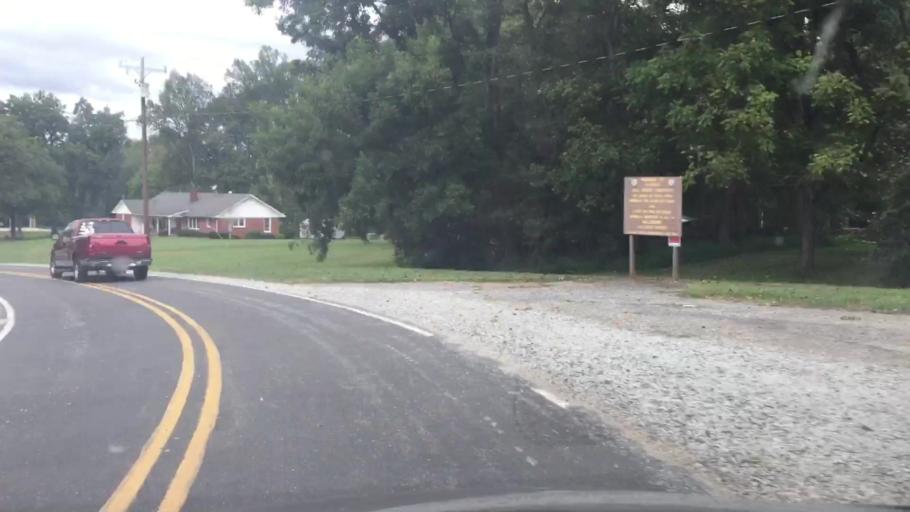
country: US
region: North Carolina
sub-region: Rowan County
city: China Grove
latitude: 35.6475
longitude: -80.6374
